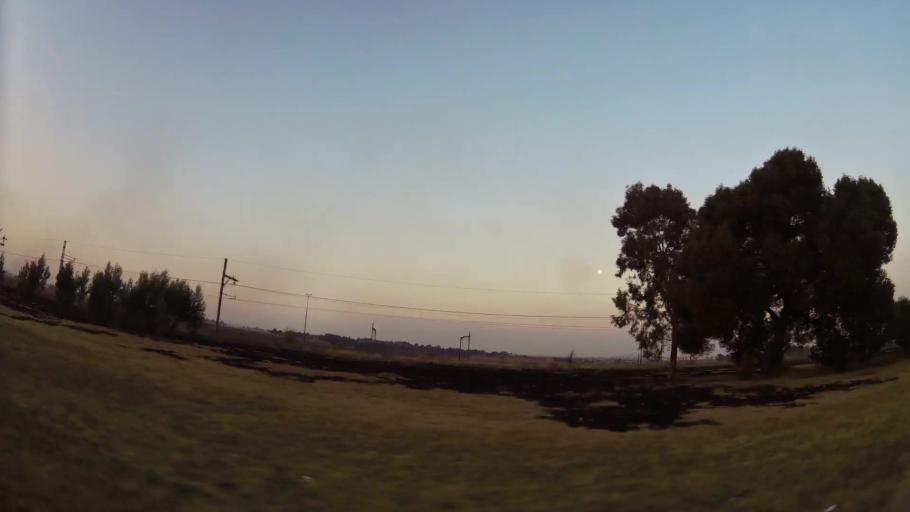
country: ZA
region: Gauteng
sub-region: Ekurhuleni Metropolitan Municipality
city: Nigel
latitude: -26.3477
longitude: 28.4409
